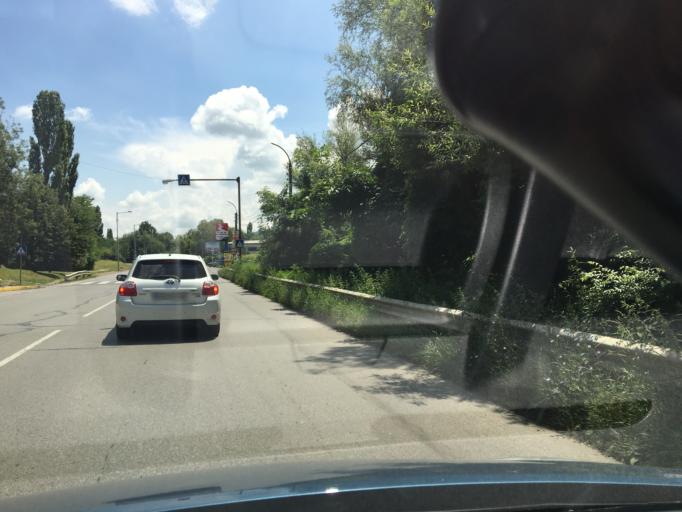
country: BG
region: Sofia-Capital
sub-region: Stolichna Obshtina
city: Sofia
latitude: 42.6603
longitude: 23.3053
